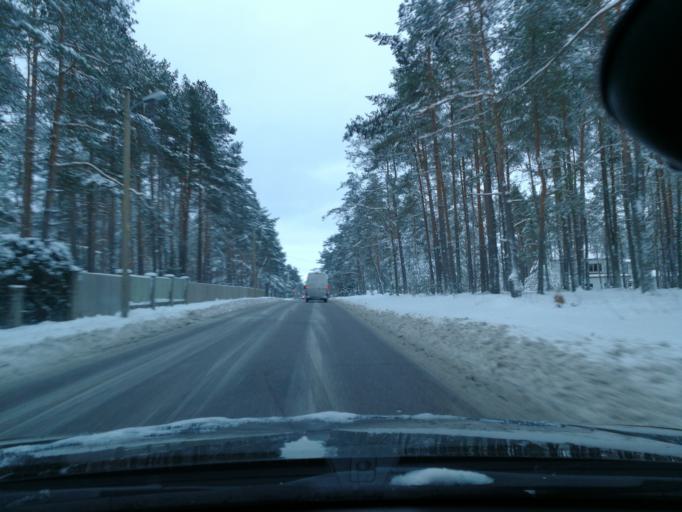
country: EE
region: Harju
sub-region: Saue vald
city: Laagri
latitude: 59.3765
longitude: 24.6716
